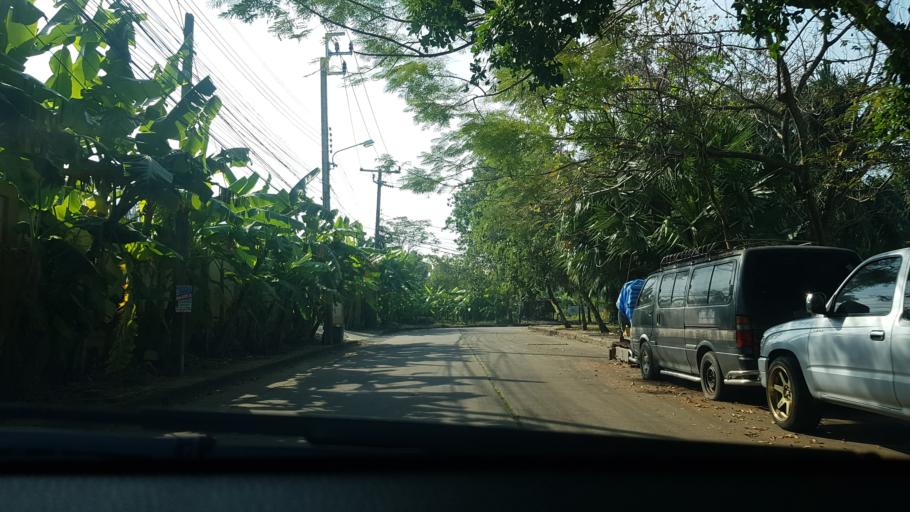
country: TH
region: Bangkok
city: Thawi Watthana
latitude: 13.7887
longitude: 100.3804
